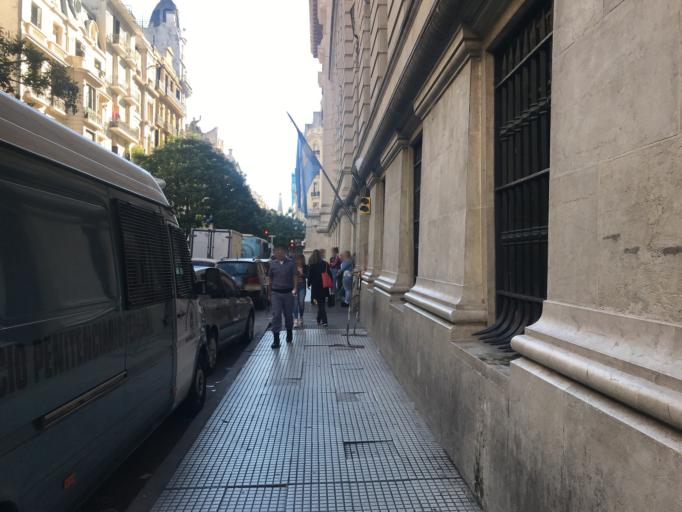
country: AR
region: Buenos Aires F.D.
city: Buenos Aires
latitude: -34.6027
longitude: -58.3855
